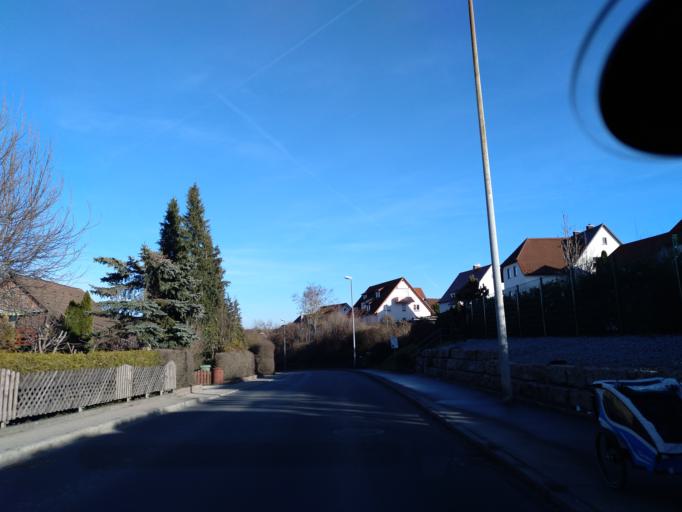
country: DE
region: Baden-Wuerttemberg
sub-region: Regierungsbezirk Stuttgart
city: Vellberg
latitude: 49.0855
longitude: 9.8764
